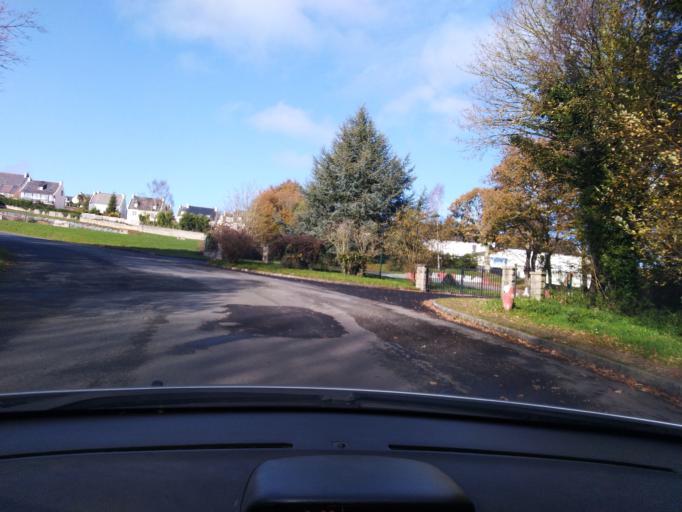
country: FR
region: Brittany
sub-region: Departement du Finistere
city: Guerlesquin
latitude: 48.5145
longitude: -3.5921
